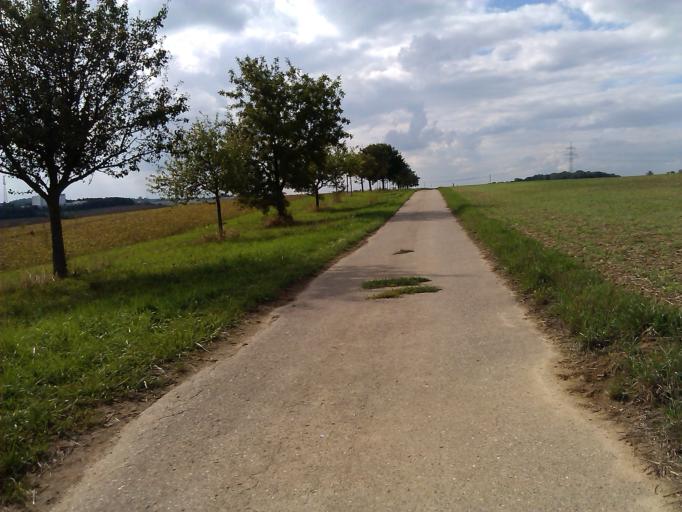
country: DE
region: Baden-Wuerttemberg
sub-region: Regierungsbezirk Stuttgart
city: Untereisesheim
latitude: 49.1913
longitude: 9.1794
